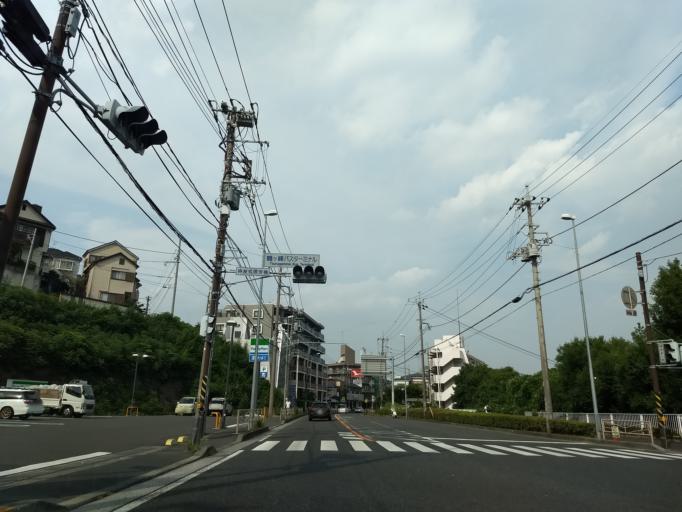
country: JP
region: Kanagawa
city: Minami-rinkan
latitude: 35.4776
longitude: 139.5467
